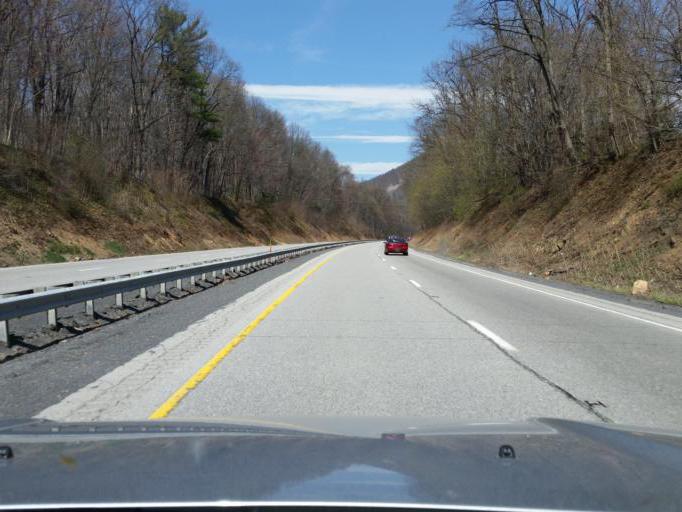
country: US
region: Pennsylvania
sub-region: Mifflin County
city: Yeagertown
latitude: 40.6403
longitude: -77.5852
